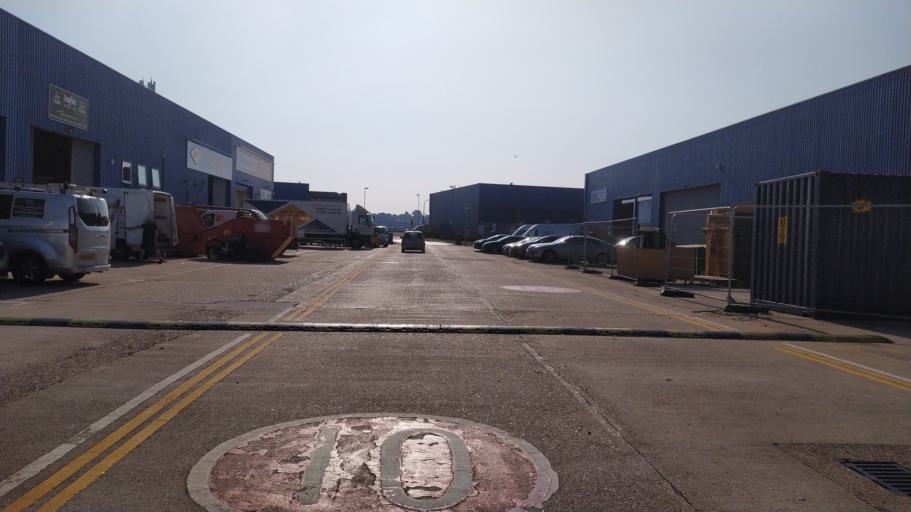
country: GB
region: England
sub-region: Southampton
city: Southampton
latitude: 50.9171
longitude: -1.3863
